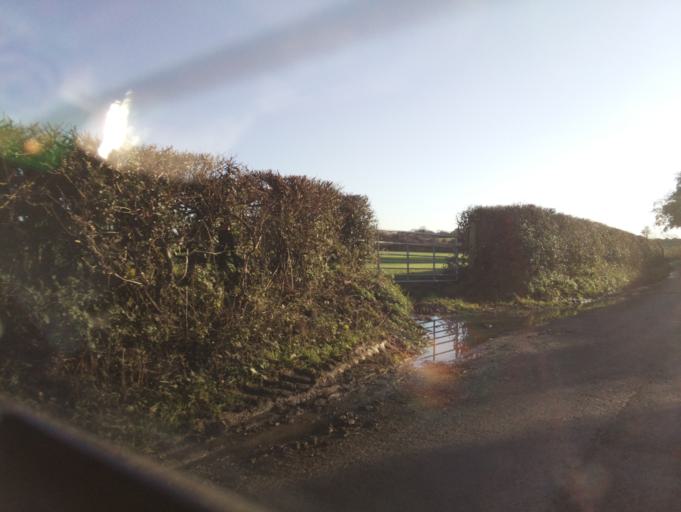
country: GB
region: England
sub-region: Somerset
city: Milborne Port
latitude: 50.9946
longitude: -2.4585
